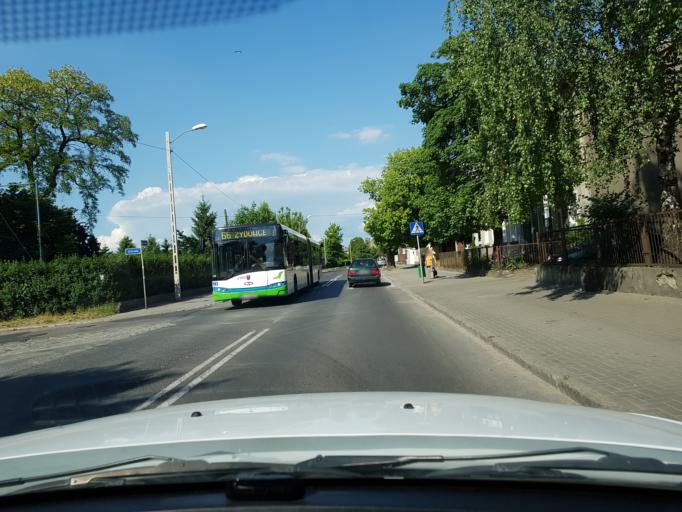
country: PL
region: West Pomeranian Voivodeship
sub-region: Szczecin
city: Szczecin
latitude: 53.3647
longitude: 14.5925
